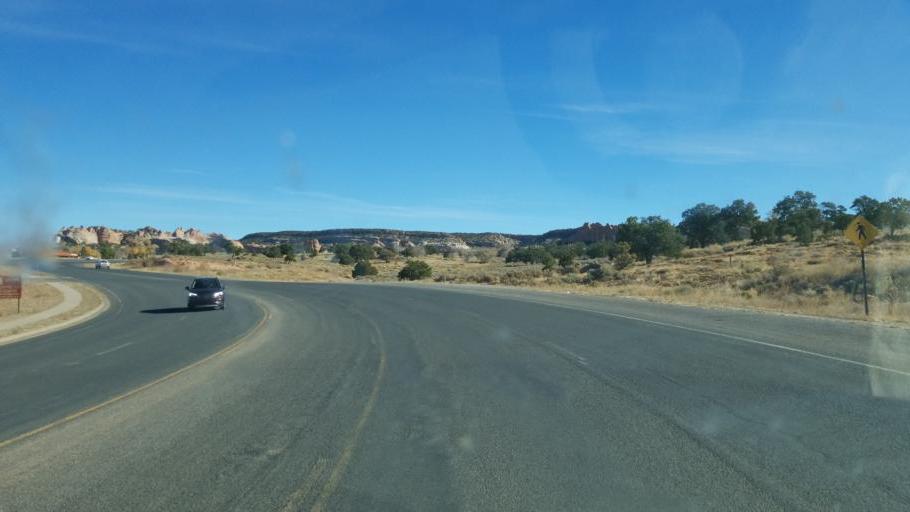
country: US
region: Arizona
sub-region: Apache County
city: Window Rock
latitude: 35.6721
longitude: -109.0572
